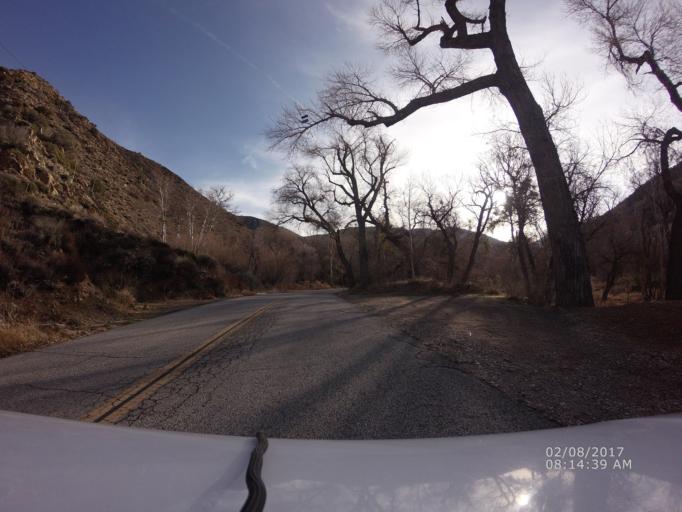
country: US
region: California
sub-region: Los Angeles County
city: Littlerock
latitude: 34.4155
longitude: -117.8334
